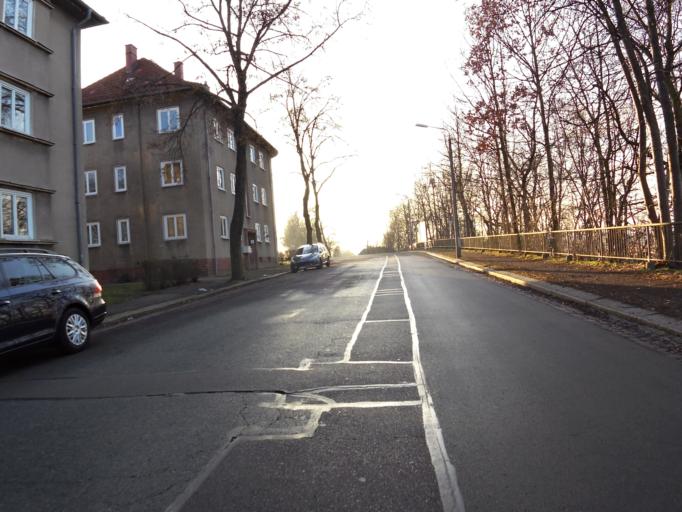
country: DE
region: Saxony
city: Glauchau
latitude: 50.8287
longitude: 12.5528
